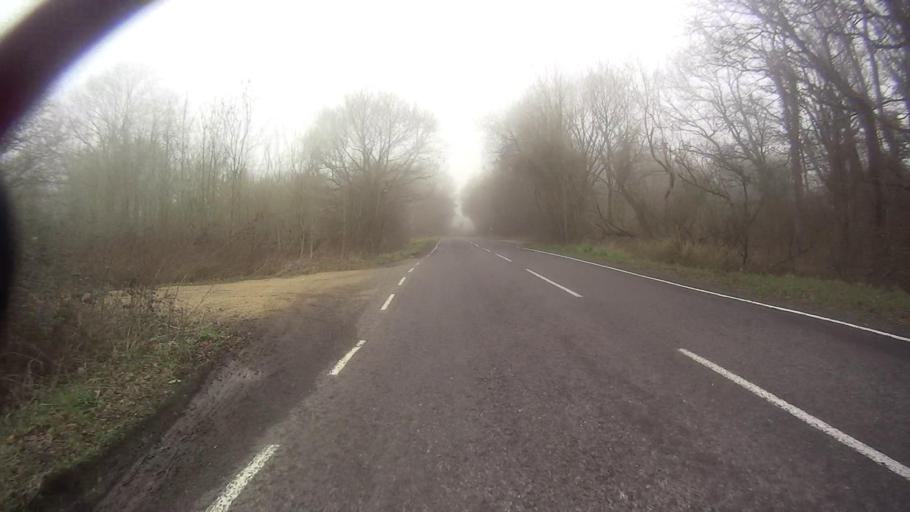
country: GB
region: England
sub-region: Surrey
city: Newdigate
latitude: 51.1430
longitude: -0.3232
